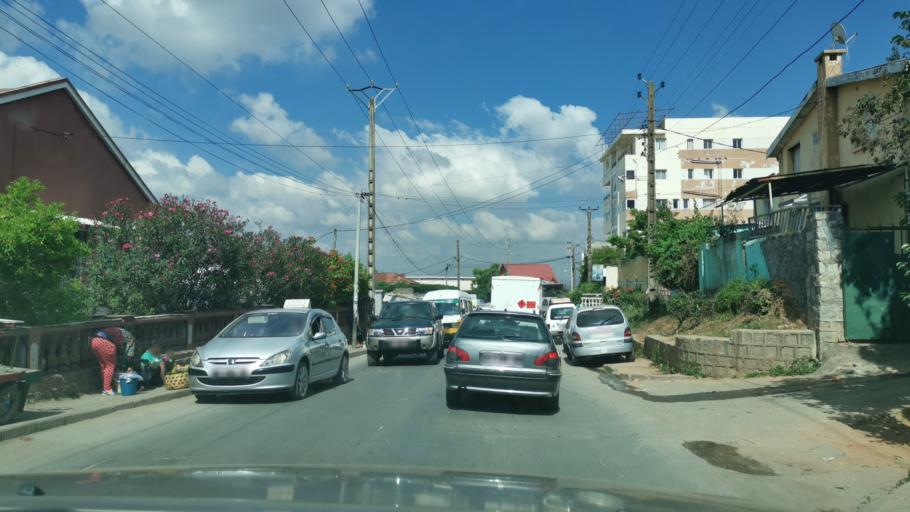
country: MG
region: Analamanga
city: Antananarivo
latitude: -18.9350
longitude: 47.5341
